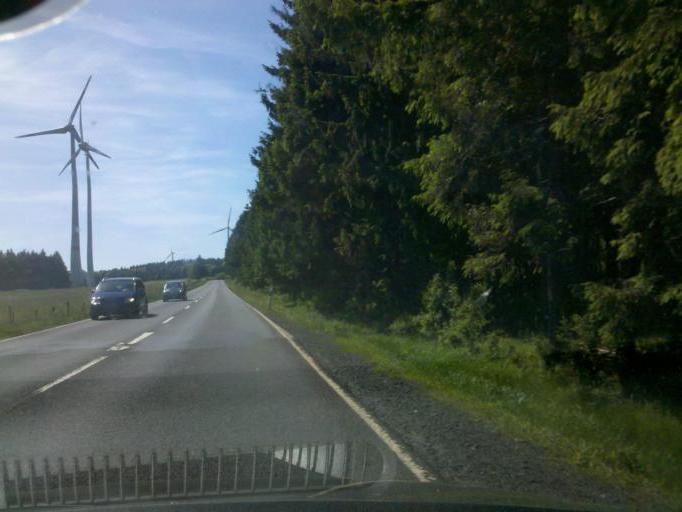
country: DE
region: Rheinland-Pfalz
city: Rehe
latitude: 50.6494
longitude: 8.1353
